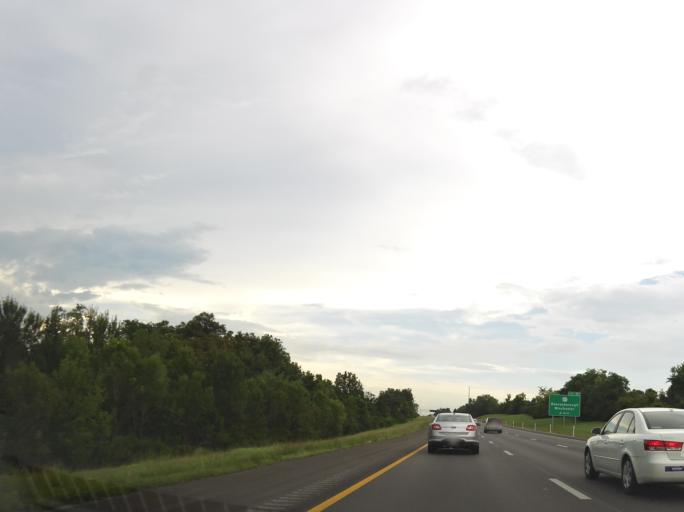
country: US
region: Kentucky
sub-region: Madison County
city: Richmond
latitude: 37.8105
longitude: -84.3237
